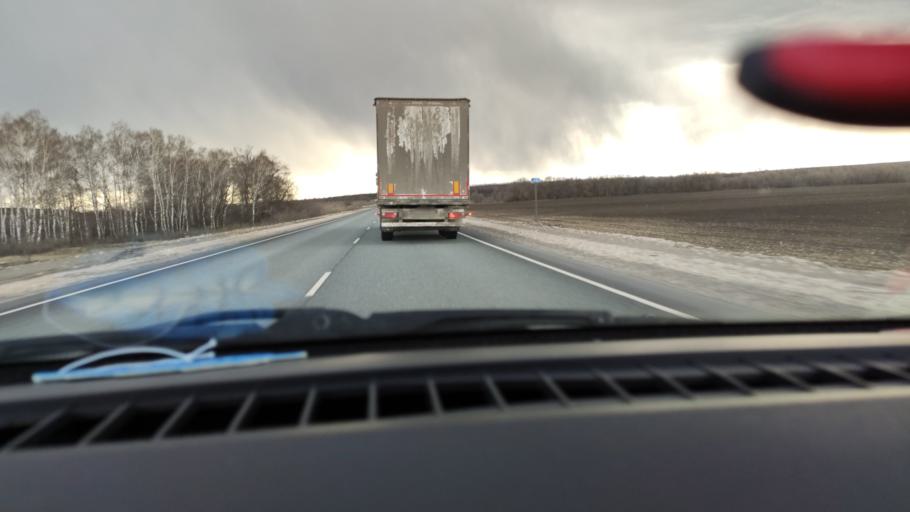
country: RU
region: Saratov
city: Yelshanka
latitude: 51.8517
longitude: 46.4905
